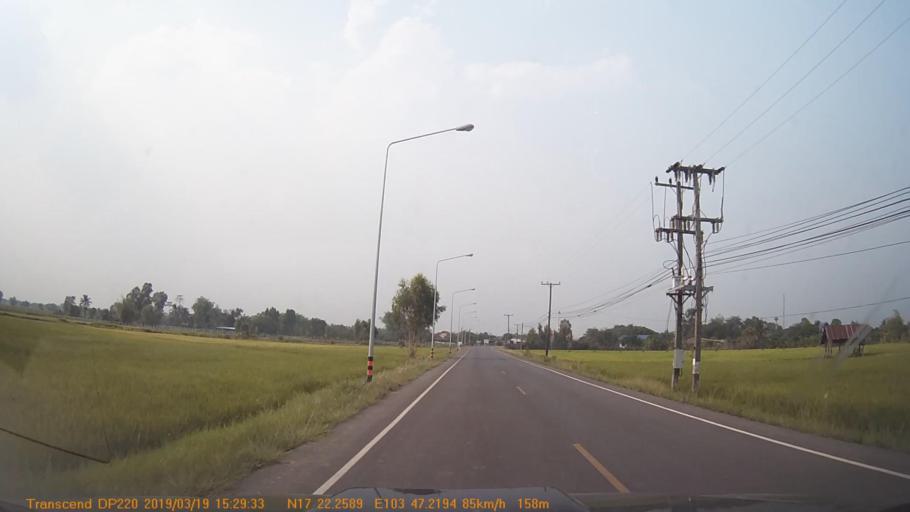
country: TH
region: Sakon Nakhon
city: Phanna Nikhom
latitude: 17.3714
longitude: 103.7869
